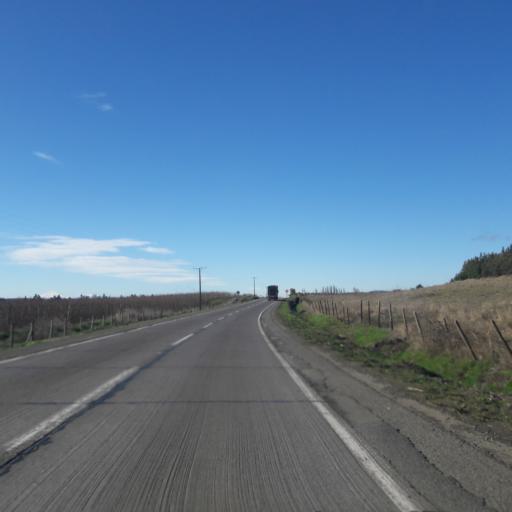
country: CL
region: Araucania
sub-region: Provincia de Malleco
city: Angol
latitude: -37.7453
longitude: -72.5977
